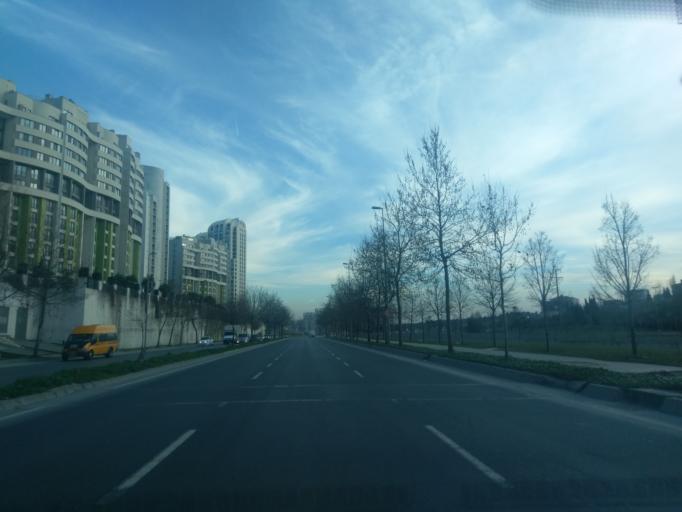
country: TR
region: Istanbul
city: Basaksehir
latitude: 41.0475
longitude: 28.7587
